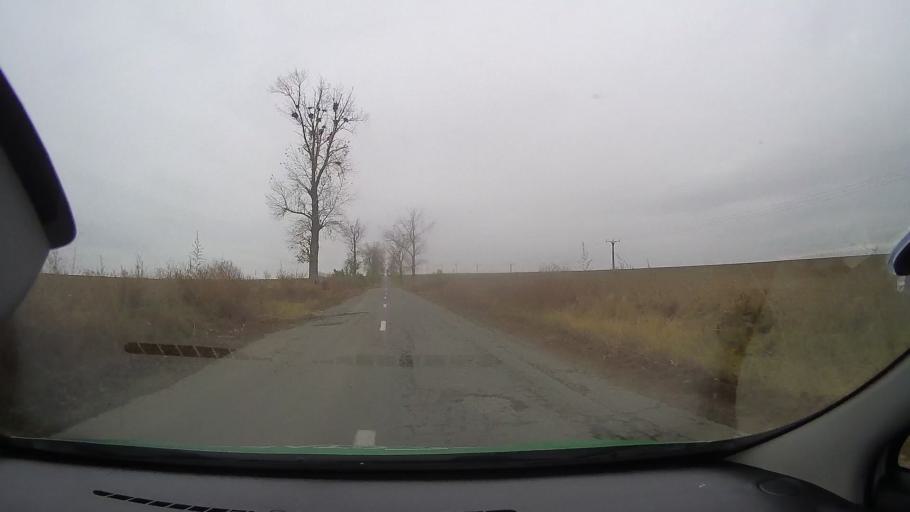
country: RO
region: Constanta
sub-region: Comuna Pantelimon
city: Pantelimon
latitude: 44.5571
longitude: 28.3241
